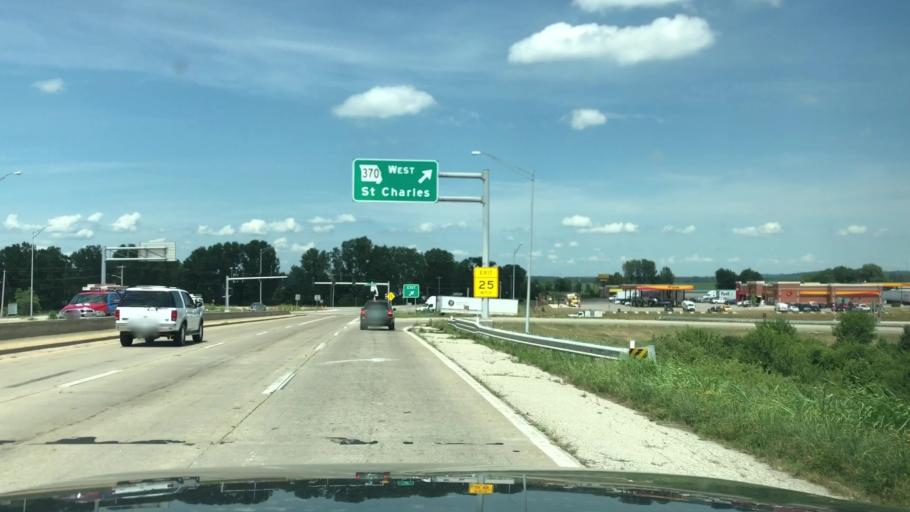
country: US
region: Missouri
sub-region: Saint Charles County
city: Saint Charles
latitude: 38.7928
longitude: -90.4517
